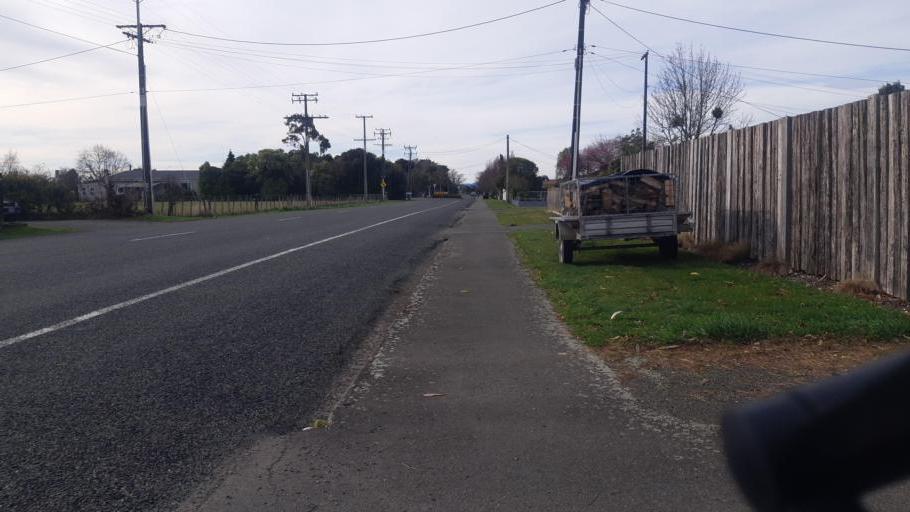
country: NZ
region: Tasman
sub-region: Tasman District
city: Brightwater
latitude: -41.3799
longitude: 173.0983
